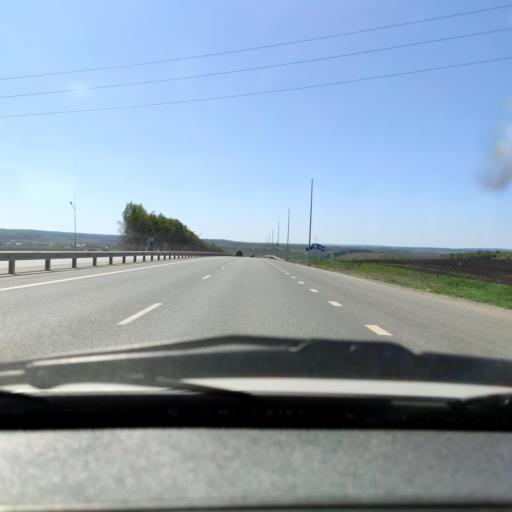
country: RU
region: Bashkortostan
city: Karmaskaly
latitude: 54.3734
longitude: 55.9154
